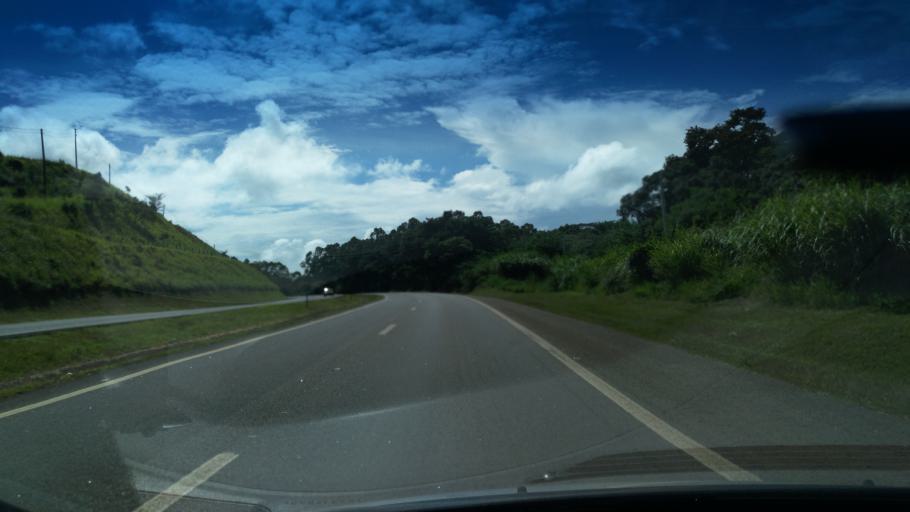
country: BR
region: Sao Paulo
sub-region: Santo Antonio Do Jardim
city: Espirito Santo do Pinhal
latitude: -22.2204
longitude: -46.7886
